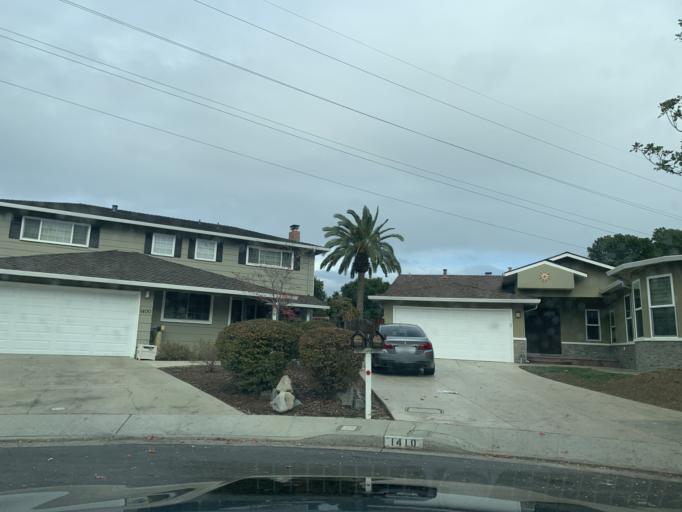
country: US
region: California
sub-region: Santa Clara County
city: Monte Sereno
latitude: 37.2677
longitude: -121.9893
